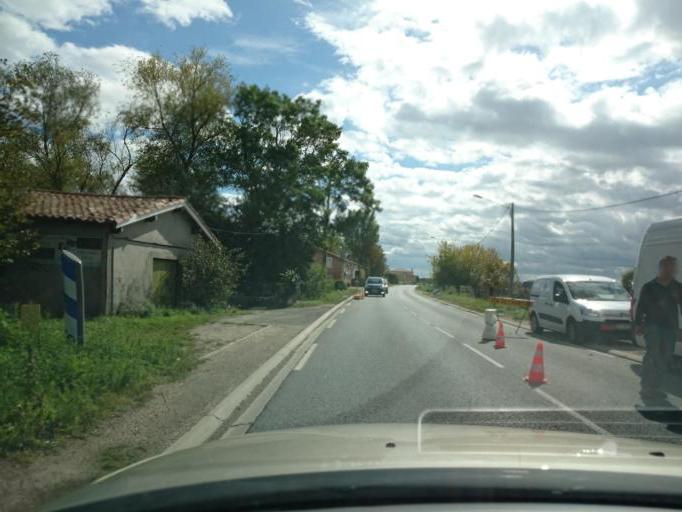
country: FR
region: Aquitaine
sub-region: Departement de la Gironde
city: Saint-Louis-de-Montferrand
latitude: 44.9334
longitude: -0.5613
